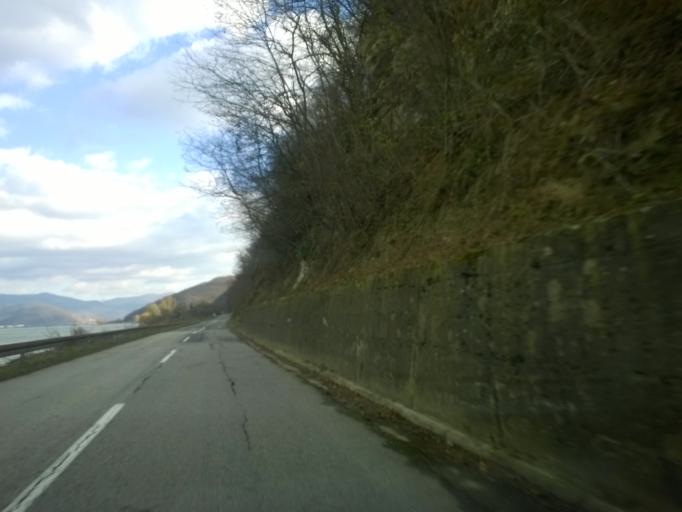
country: RO
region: Caras-Severin
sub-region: Comuna Berzasca
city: Liubcova
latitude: 44.6426
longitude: 21.8894
